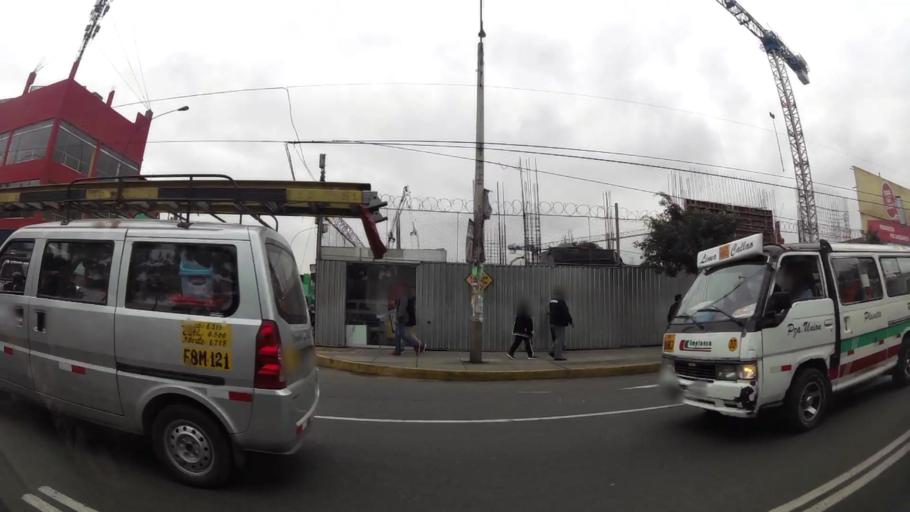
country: PE
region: Lima
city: Lima
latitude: -12.0436
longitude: -77.0484
